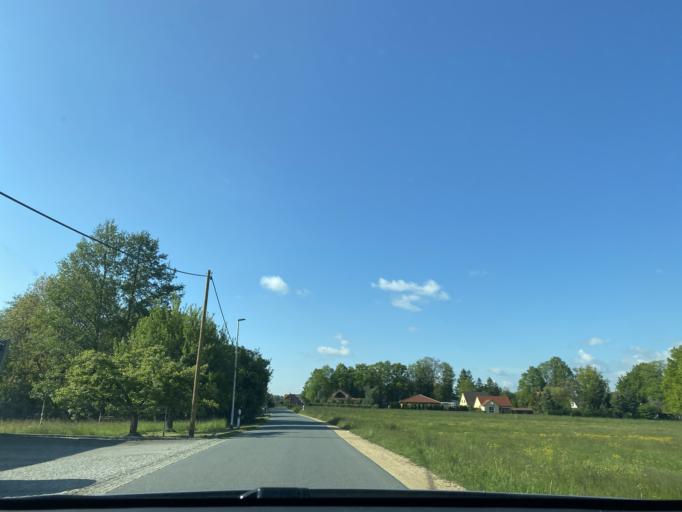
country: DE
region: Saxony
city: Reichenbach
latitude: 51.1007
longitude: 14.8319
